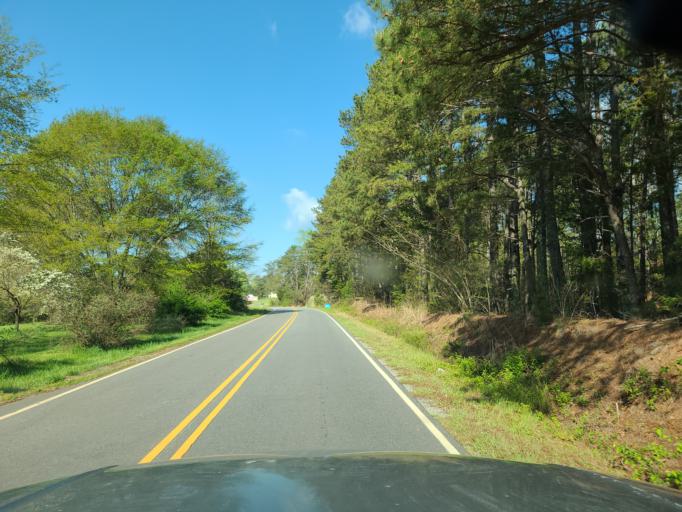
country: US
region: North Carolina
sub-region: Rutherford County
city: Spindale
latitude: 35.3975
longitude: -81.9028
